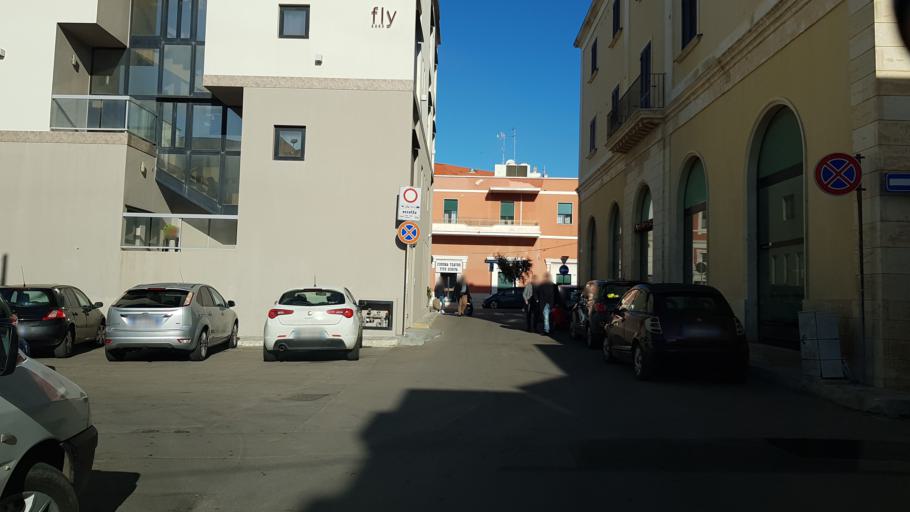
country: IT
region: Apulia
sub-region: Provincia di Lecce
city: Gallipoli
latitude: 40.0556
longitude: 17.9847
